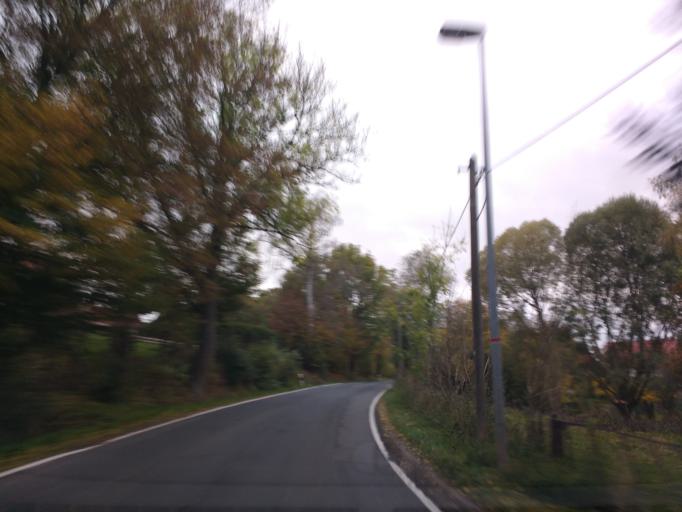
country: DE
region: Thuringia
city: Grossbodungen
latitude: 51.5108
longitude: 10.5130
